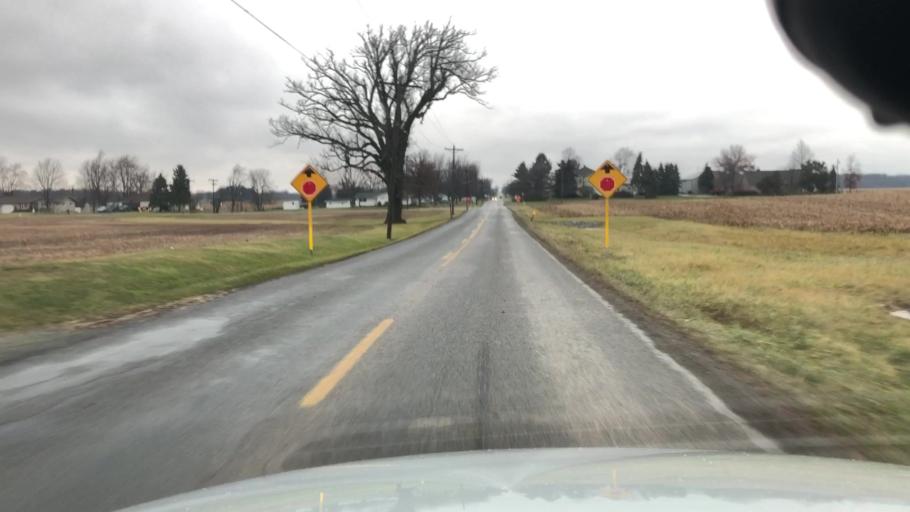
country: US
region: Ohio
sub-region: Allen County
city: Lima
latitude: 40.7875
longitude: -84.0131
